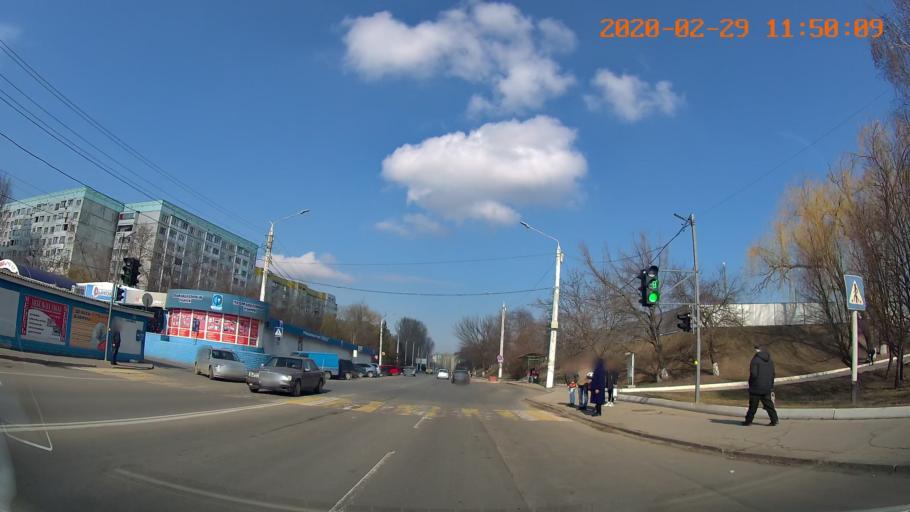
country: MD
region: Telenesti
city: Ribnita
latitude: 47.7560
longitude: 28.9914
